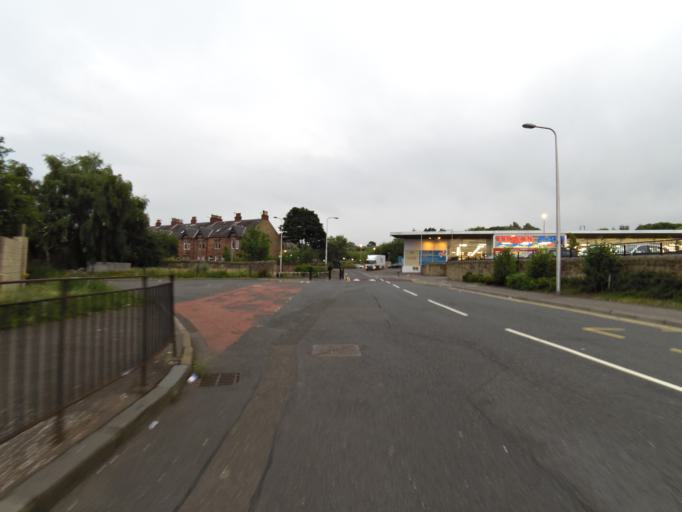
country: GB
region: Scotland
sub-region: East Lothian
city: Musselburgh
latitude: 55.9398
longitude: -3.0550
